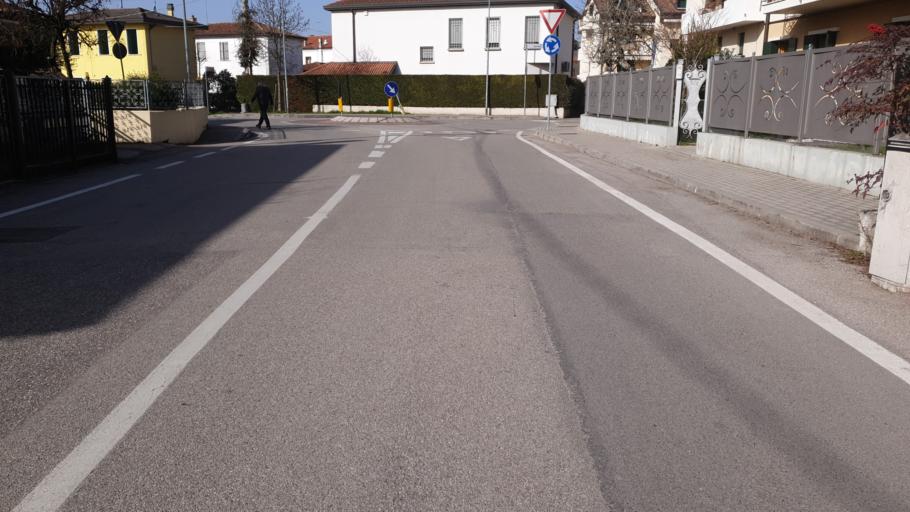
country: IT
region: Veneto
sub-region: Provincia di Padova
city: Cadoneghe
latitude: 45.4354
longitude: 11.9300
